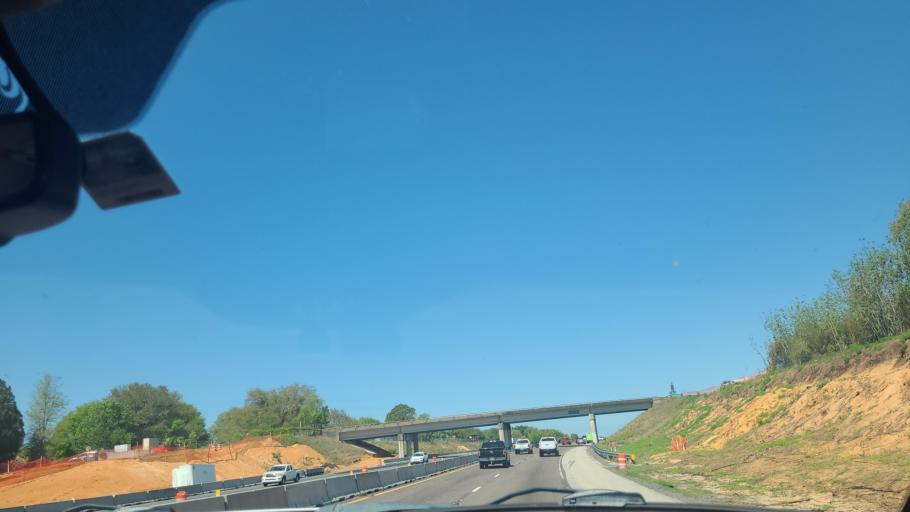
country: US
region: Florida
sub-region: Lake County
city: Montverde
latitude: 28.5607
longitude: -81.6801
